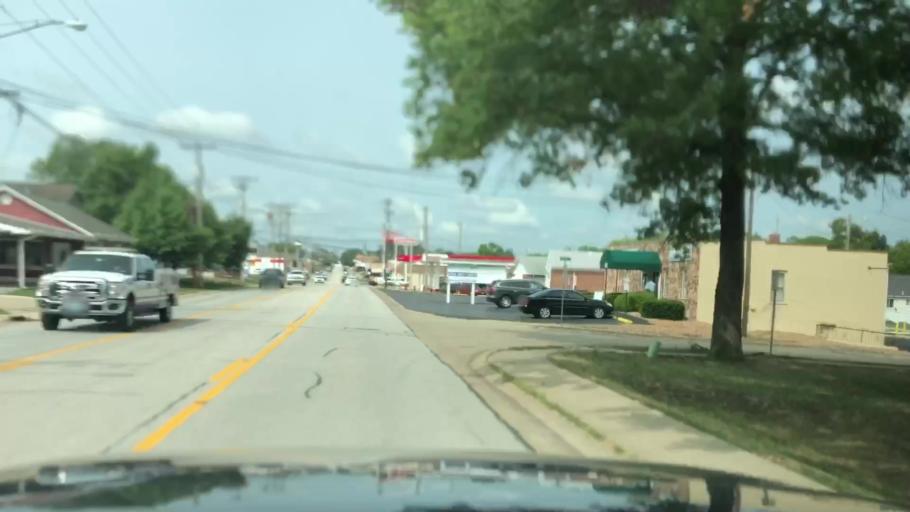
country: US
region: Missouri
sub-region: Saint Charles County
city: Wentzville
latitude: 38.8129
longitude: -90.8491
